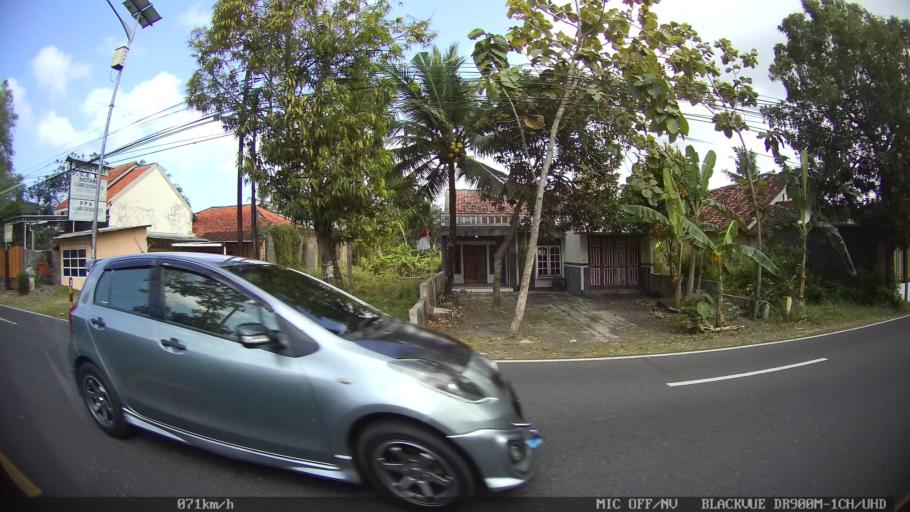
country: ID
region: Daerah Istimewa Yogyakarta
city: Srandakan
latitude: -7.8886
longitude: 110.1300
